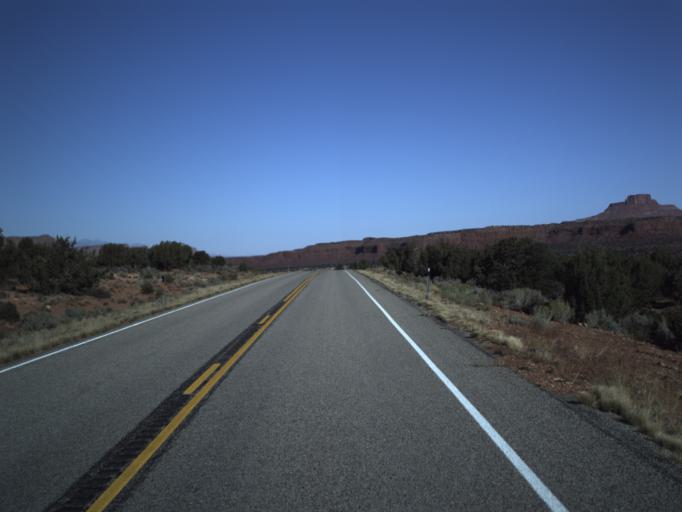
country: US
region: Utah
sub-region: San Juan County
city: Blanding
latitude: 37.6525
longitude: -110.1720
